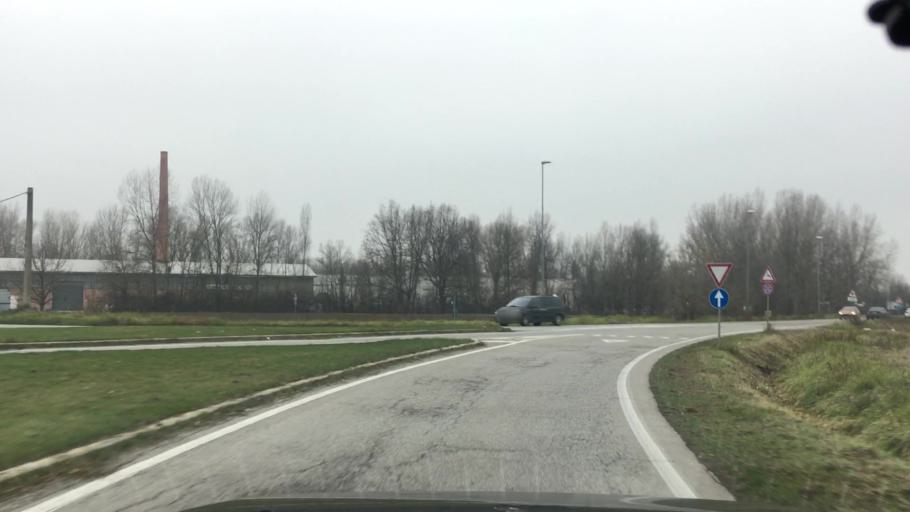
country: IT
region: Emilia-Romagna
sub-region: Provincia di Bologna
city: San Giovanni in Persiceto
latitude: 44.6283
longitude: 11.2065
